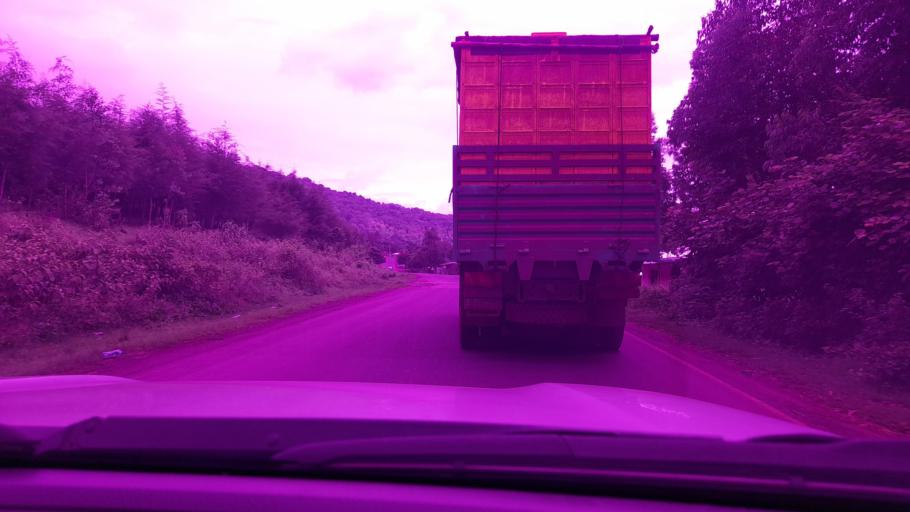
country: ET
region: Oromiya
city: Jima
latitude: 7.6612
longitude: 36.8772
